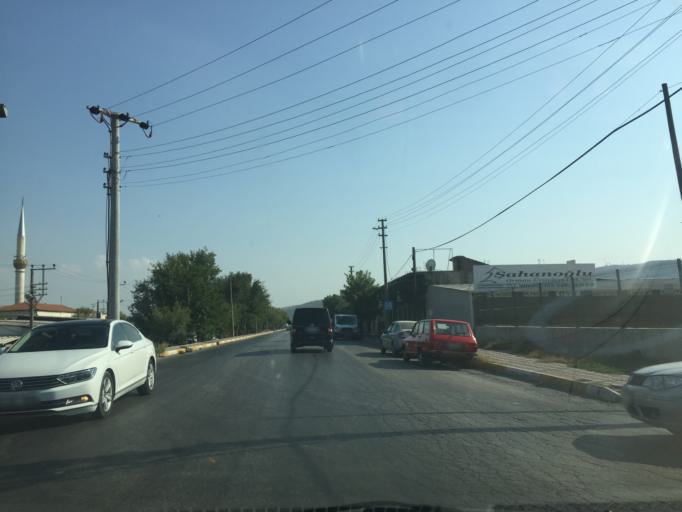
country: TR
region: Manisa
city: Akhisar
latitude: 38.9077
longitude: 27.8370
